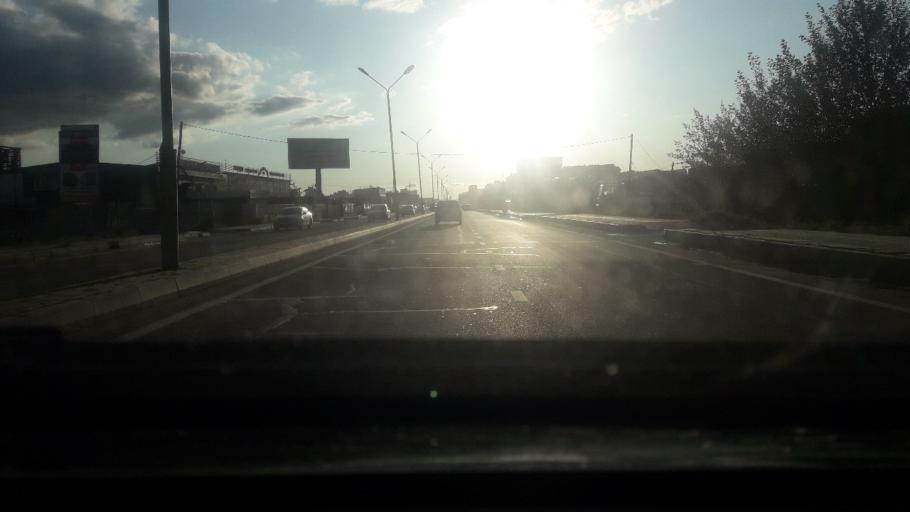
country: MN
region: Ulaanbaatar
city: Ulaanbaatar
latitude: 47.9079
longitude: 106.9647
